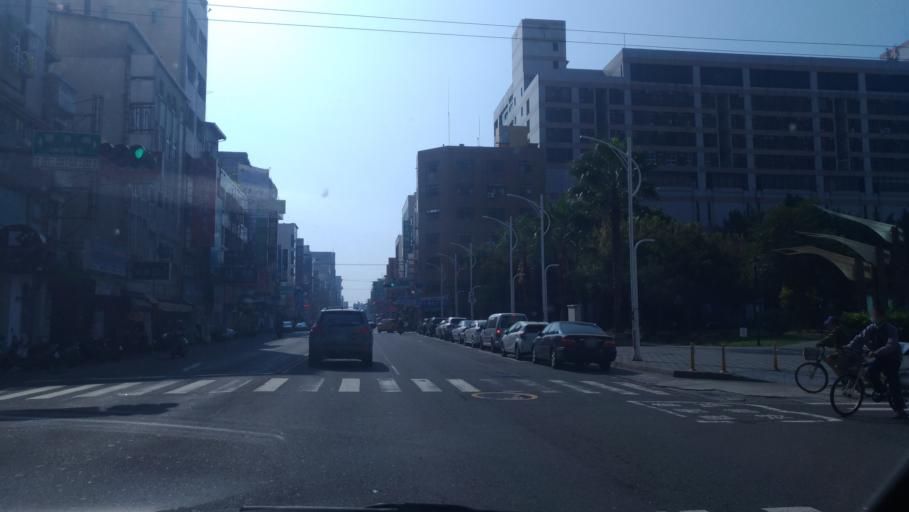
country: TW
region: Taiwan
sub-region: Chiayi
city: Jiayi Shi
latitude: 23.4772
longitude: 120.4464
